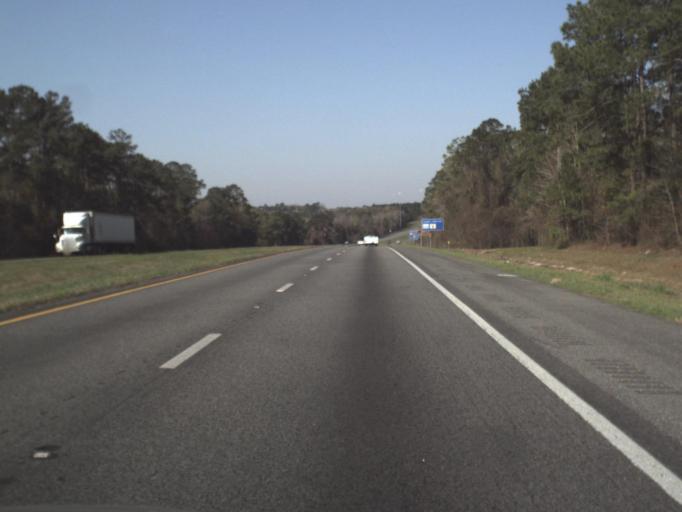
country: US
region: Florida
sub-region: Jefferson County
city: Monticello
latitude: 30.4735
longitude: -83.8730
